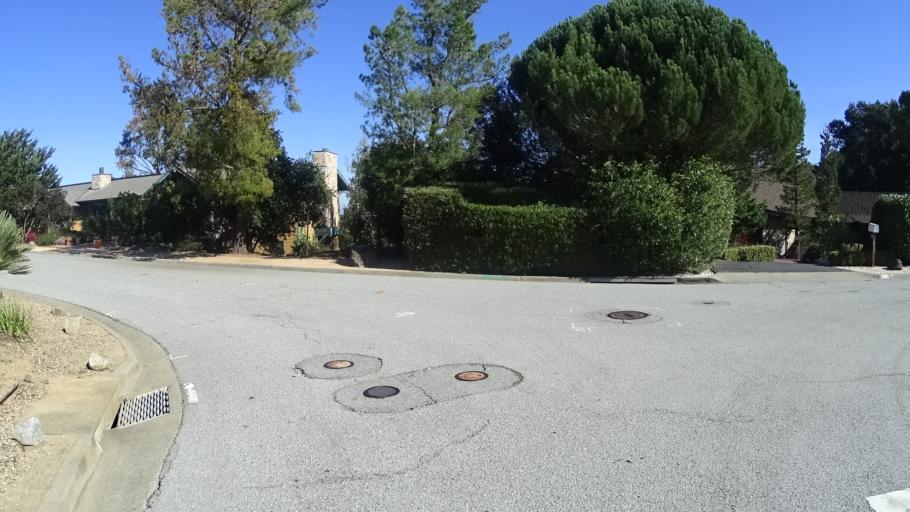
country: US
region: California
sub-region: San Mateo County
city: Hillsborough
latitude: 37.5589
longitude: -122.3793
